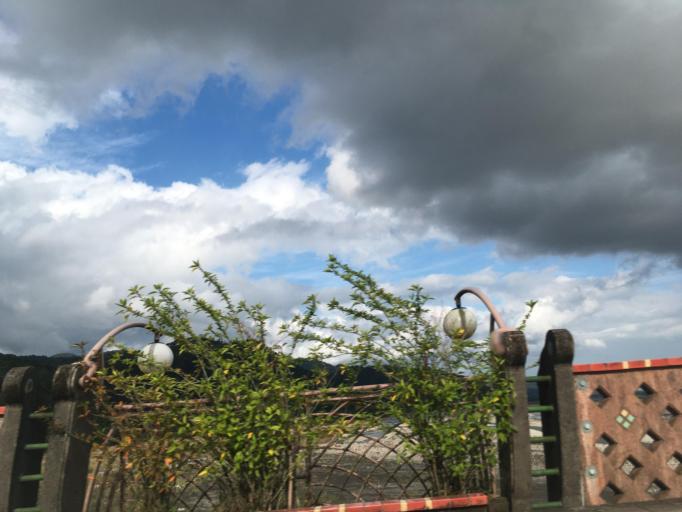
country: TW
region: Taiwan
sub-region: Yilan
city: Yilan
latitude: 24.6698
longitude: 121.6091
